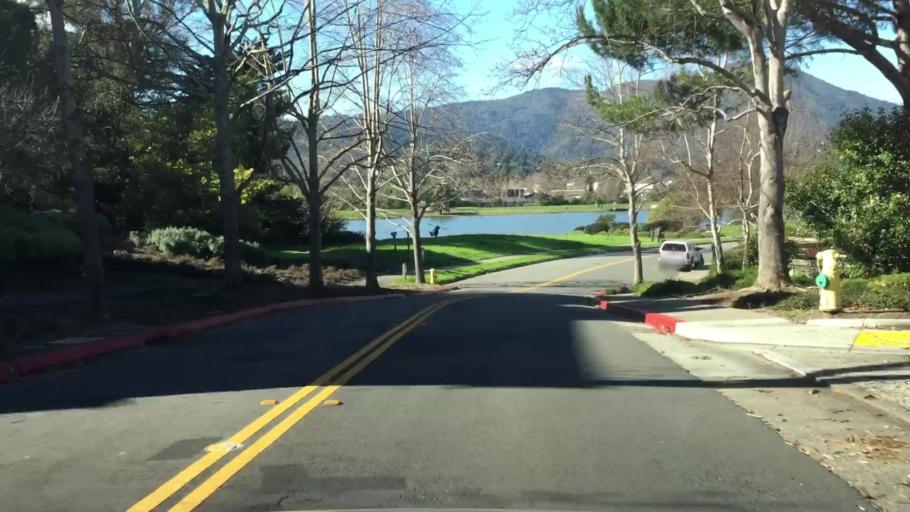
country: US
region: California
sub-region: Marin County
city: Strawberry
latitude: 37.8940
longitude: -122.5213
